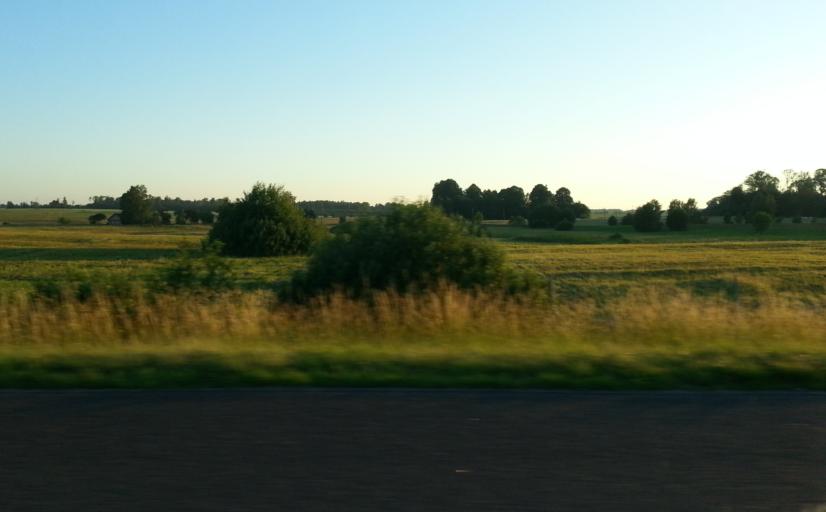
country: LT
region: Vilnius County
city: Ukmerge
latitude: 55.1518
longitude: 24.8232
